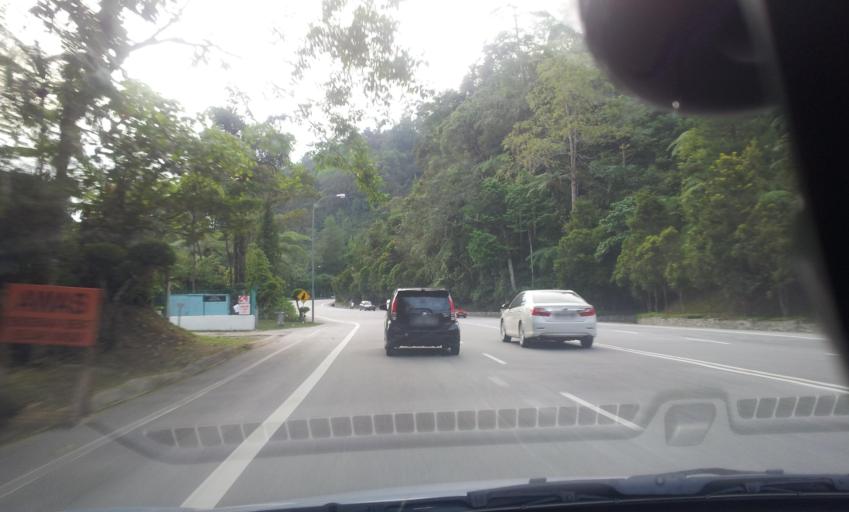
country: MY
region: Pahang
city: Kampung Bukit Tinggi, Bentong
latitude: 3.4081
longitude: 101.7843
